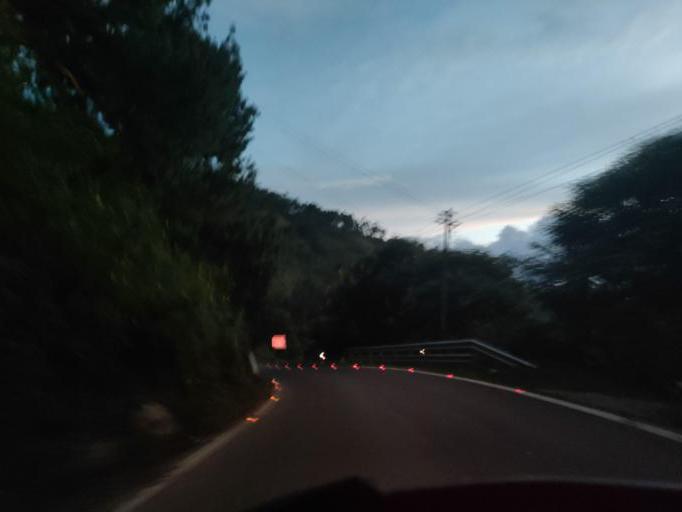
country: IN
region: Tamil Nadu
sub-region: Dindigul
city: Kodaikanal
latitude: 10.2863
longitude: 77.5396
